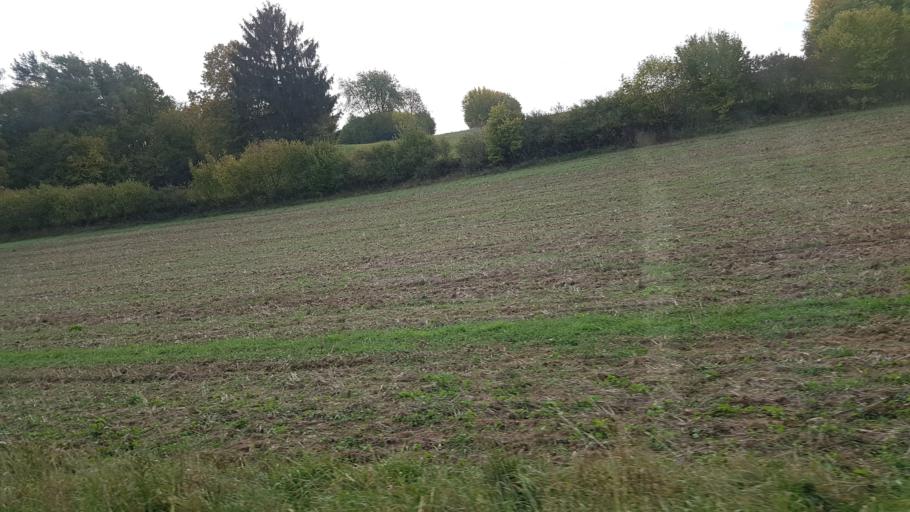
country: DE
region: Bavaria
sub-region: Upper Franconia
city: Waischenfeld
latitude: 49.8433
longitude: 11.3380
